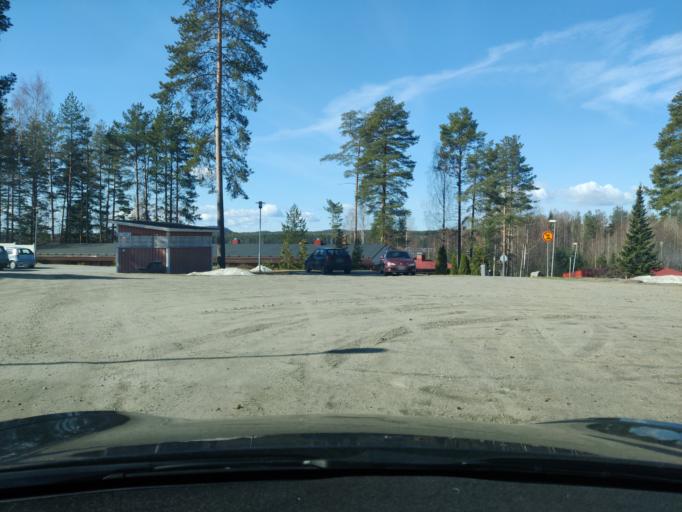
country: FI
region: Northern Savo
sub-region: Kuopio
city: Vehmersalmi
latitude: 62.7587
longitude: 28.0339
